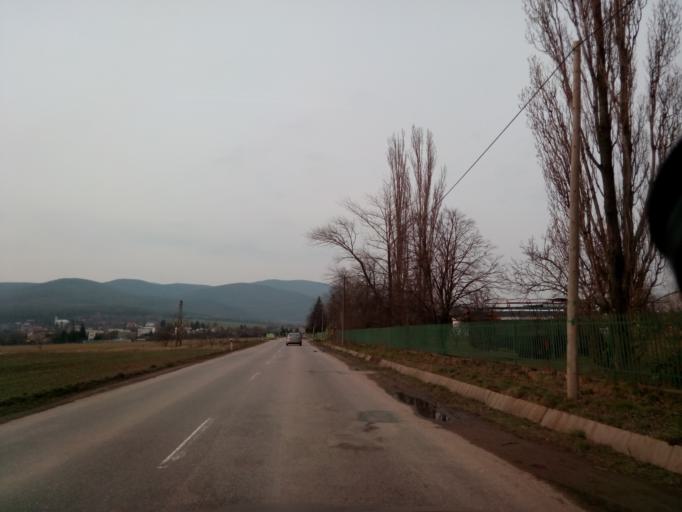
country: SK
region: Kosicky
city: Secovce
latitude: 48.6404
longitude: 21.5796
